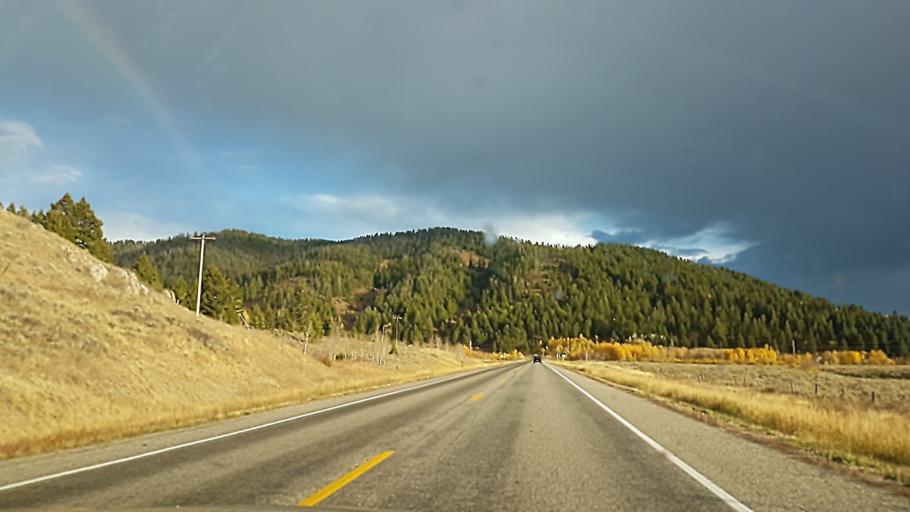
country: US
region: Montana
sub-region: Gallatin County
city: West Yellowstone
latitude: 44.6387
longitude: -111.3329
